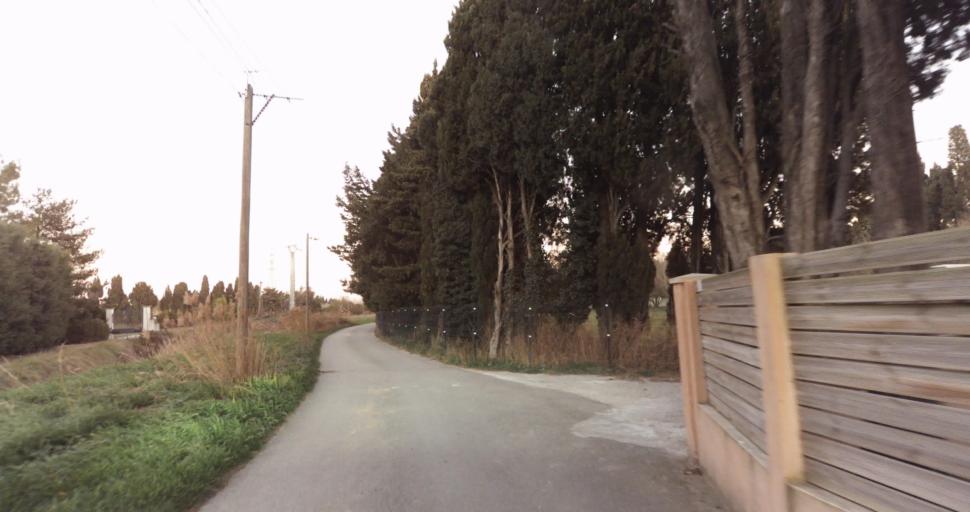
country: FR
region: Provence-Alpes-Cote d'Azur
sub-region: Departement des Bouches-du-Rhone
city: Rognonas
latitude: 43.9123
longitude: 4.7857
